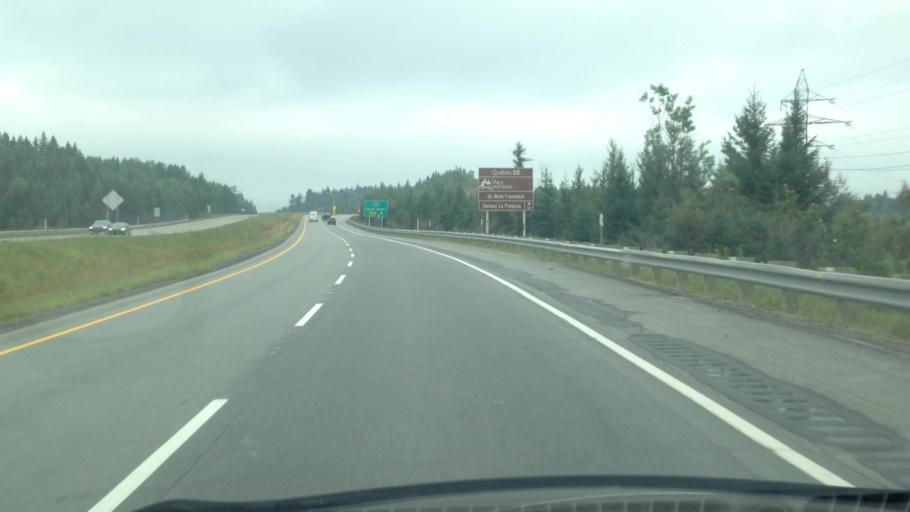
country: CA
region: Quebec
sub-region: Laurentides
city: Sainte-Agathe-des-Monts
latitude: 46.0615
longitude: -74.2794
